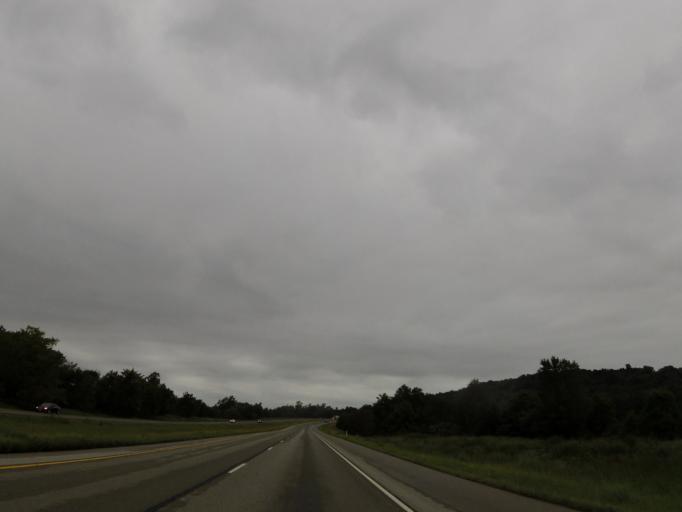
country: US
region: Illinois
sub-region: Johnson County
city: Vienna
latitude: 37.3354
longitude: -88.7803
